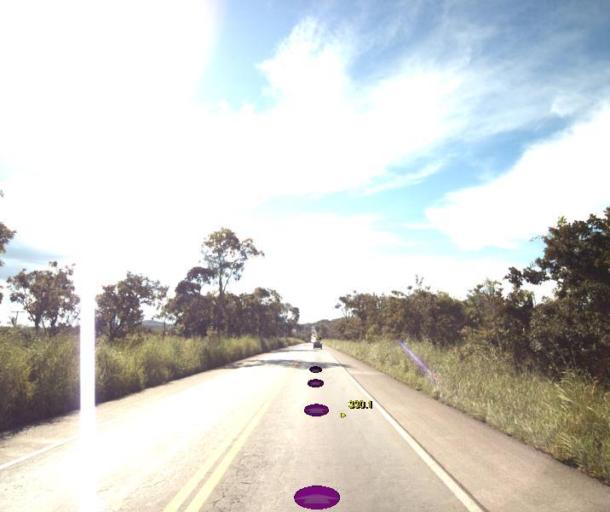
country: BR
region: Goias
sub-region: Uruana
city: Uruana
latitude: -15.5210
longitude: -49.4675
